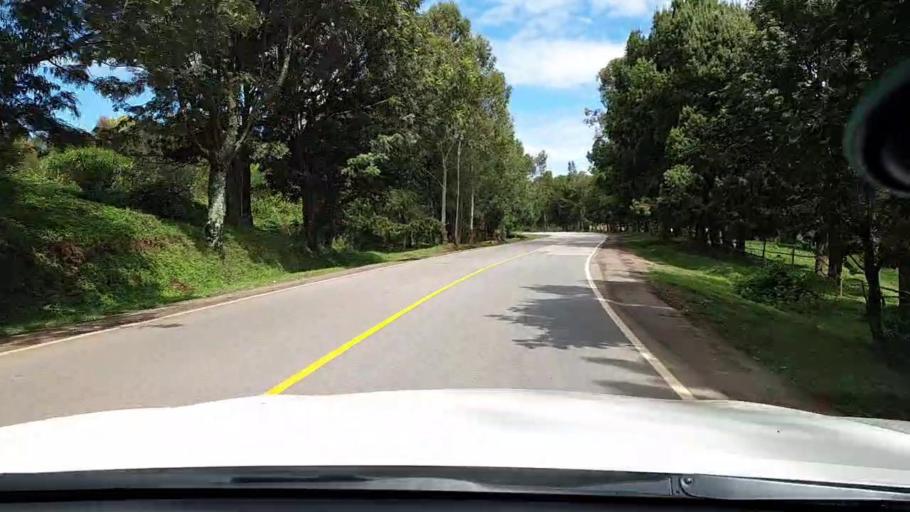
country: RW
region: Kigali
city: Kigali
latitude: -1.8226
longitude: 29.9420
